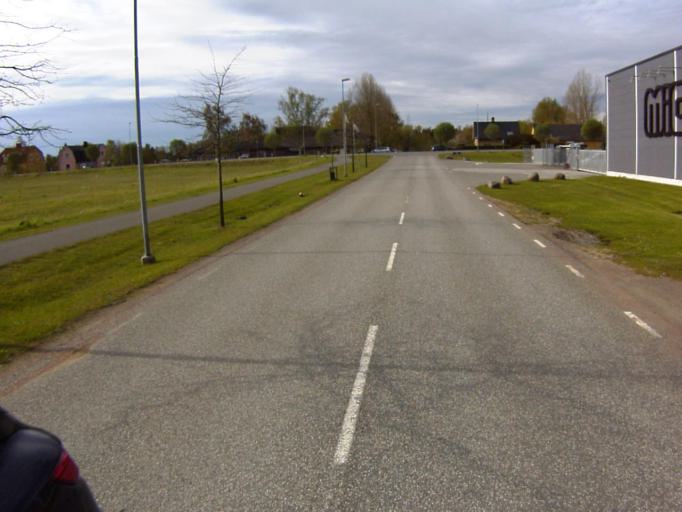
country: SE
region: Skane
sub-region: Kristianstads Kommun
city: Kristianstad
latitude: 56.0215
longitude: 14.1197
